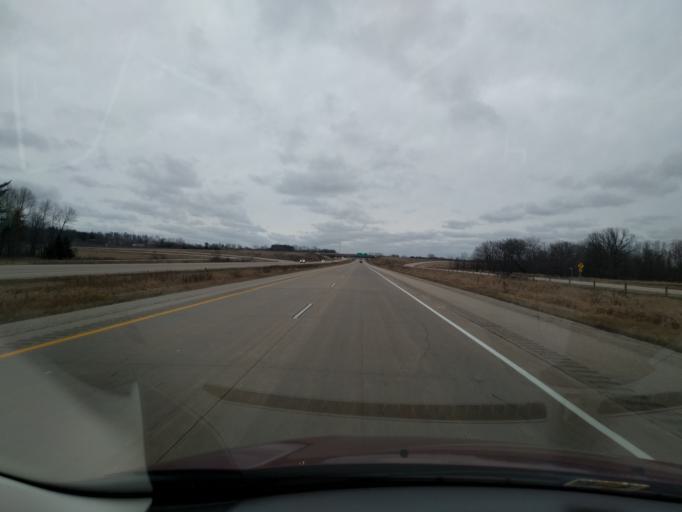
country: US
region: Wisconsin
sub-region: Winnebago County
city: Winneconne
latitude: 44.2340
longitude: -88.7472
